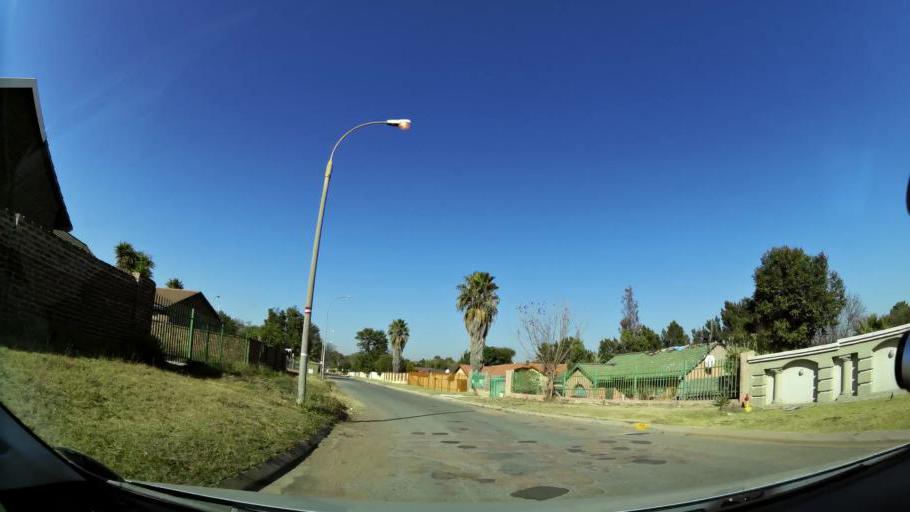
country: ZA
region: Gauteng
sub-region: City of Johannesburg Metropolitan Municipality
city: Modderfontein
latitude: -26.0546
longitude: 28.1965
